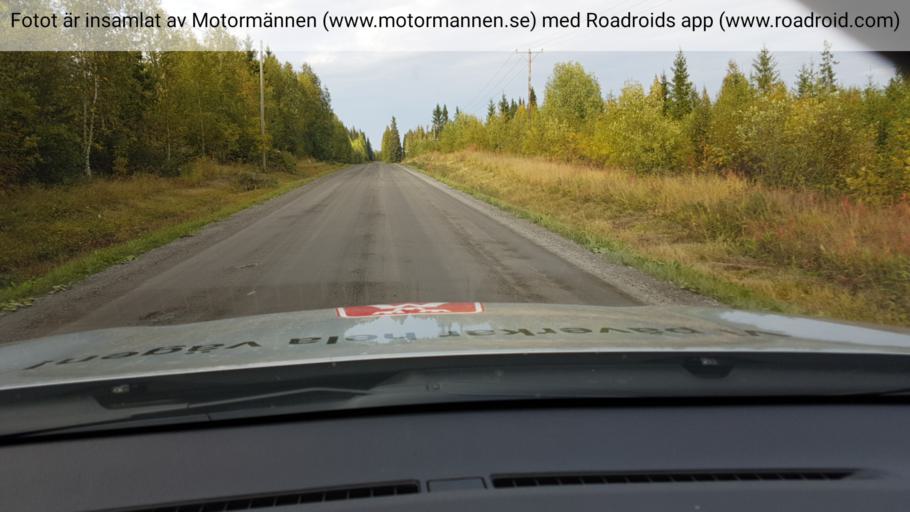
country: SE
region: Jaemtland
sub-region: Stroemsunds Kommun
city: Stroemsund
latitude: 63.9956
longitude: 15.8166
